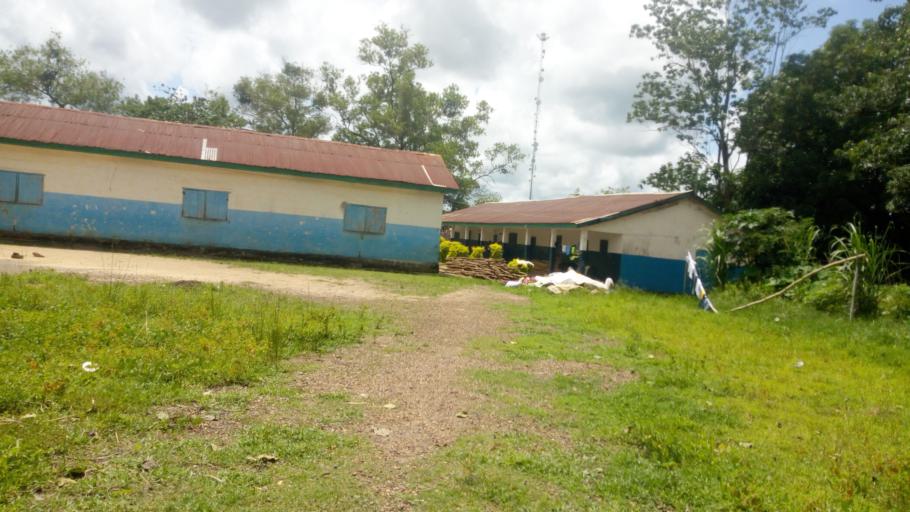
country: SL
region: Northern Province
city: Magburaka
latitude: 8.7152
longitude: -11.9502
